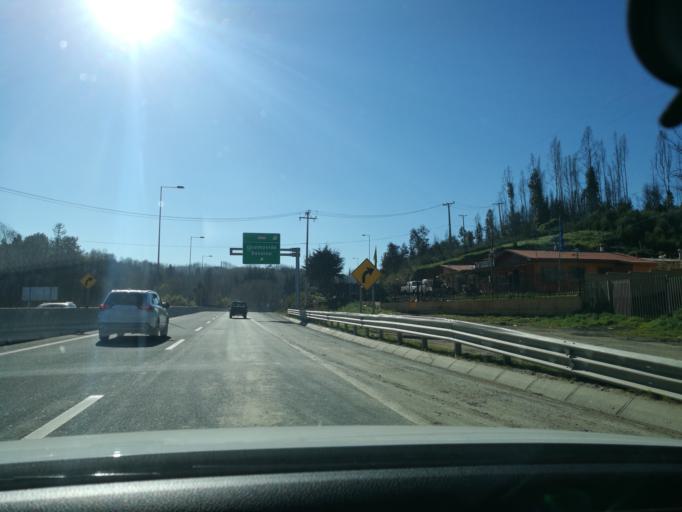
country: CL
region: Biobio
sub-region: Provincia de Concepcion
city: Chiguayante
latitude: -36.8569
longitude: -72.8809
